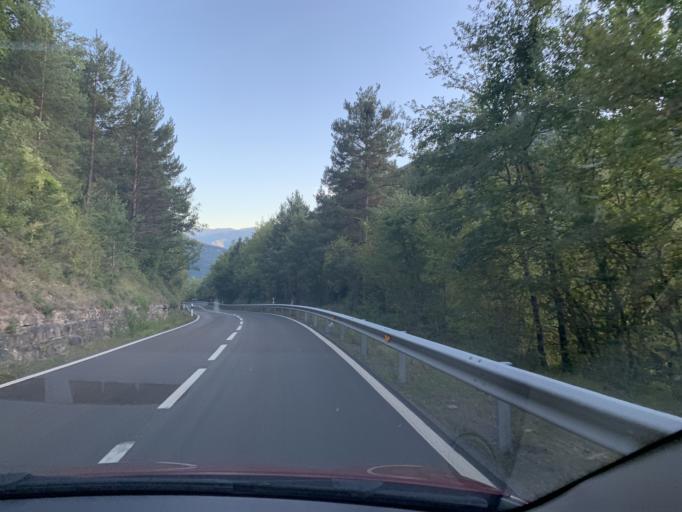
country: ES
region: Aragon
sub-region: Provincia de Huesca
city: Broto
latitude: 42.5927
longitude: -0.1184
